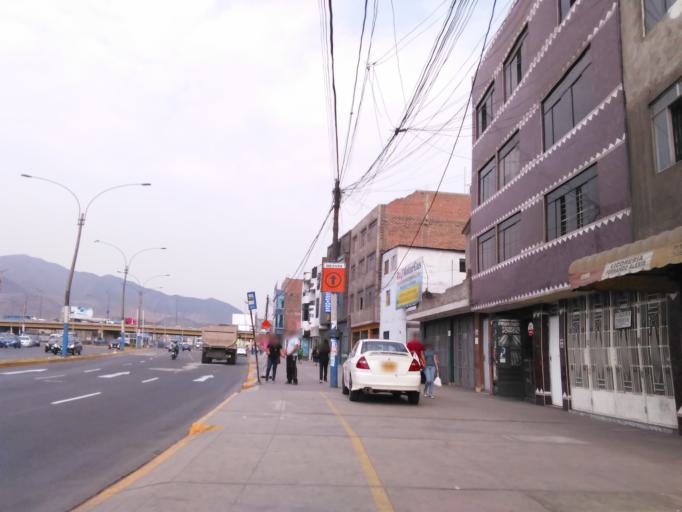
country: PE
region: Lima
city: Lima
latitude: -12.0299
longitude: -77.0598
